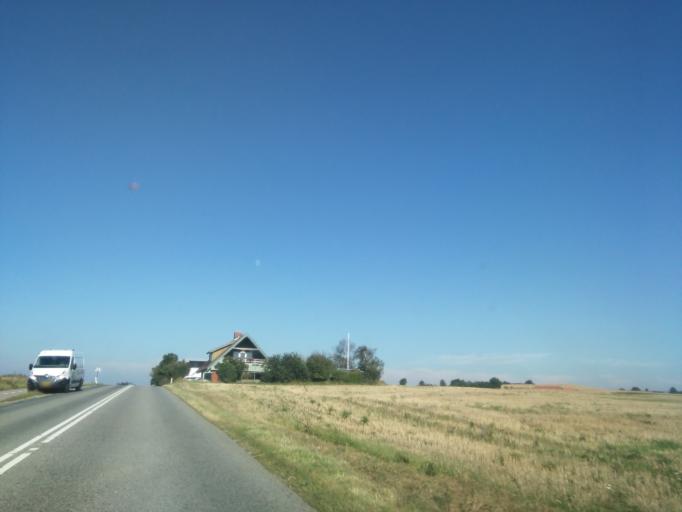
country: DK
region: Central Jutland
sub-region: Syddjurs Kommune
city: Ronde
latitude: 56.2350
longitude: 10.4907
